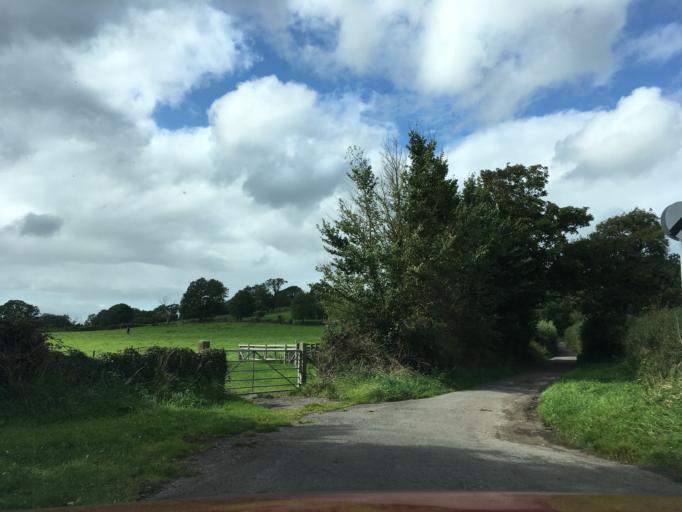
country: GB
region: England
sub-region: South Gloucestershire
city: Falfield
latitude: 51.6146
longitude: -2.4397
